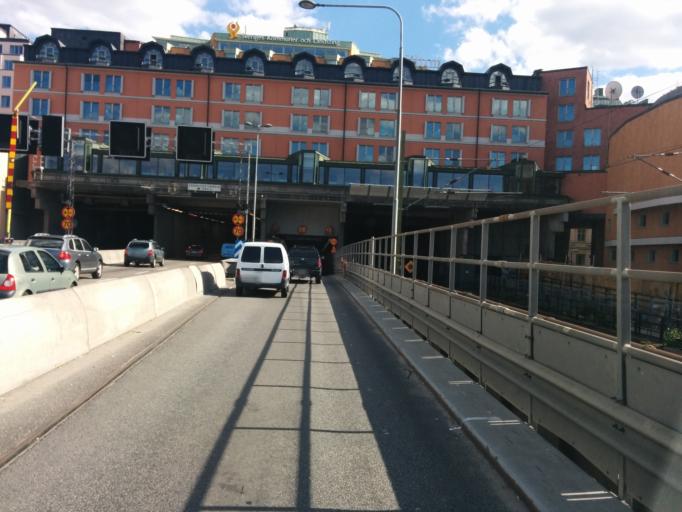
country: SE
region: Stockholm
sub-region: Stockholms Kommun
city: Stockholm
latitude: 59.3210
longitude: 18.0680
